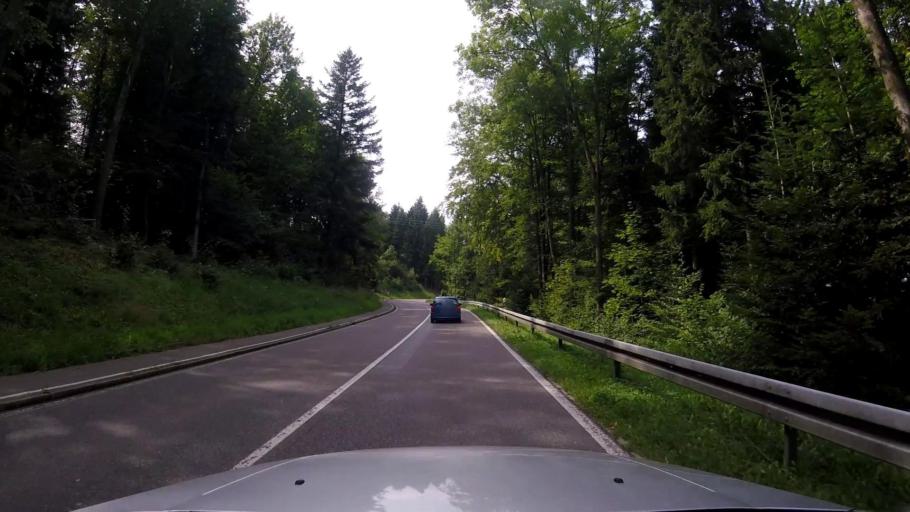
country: DE
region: Baden-Wuerttemberg
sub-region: Regierungsbezirk Stuttgart
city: Gschwend
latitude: 48.9268
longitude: 9.7343
